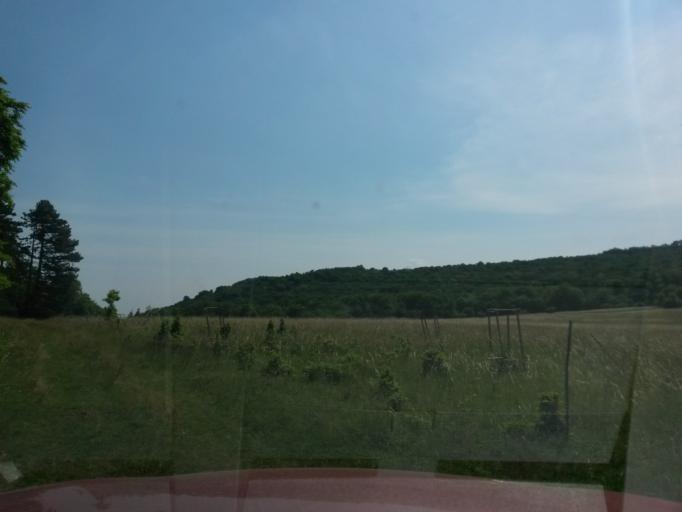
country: SK
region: Kosicky
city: Moldava nad Bodvou
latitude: 48.6461
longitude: 20.9523
